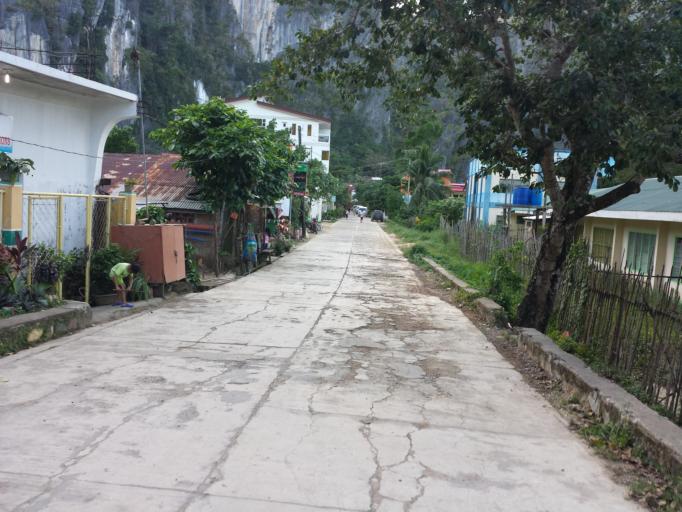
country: PH
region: Mimaropa
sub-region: Province of Palawan
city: El Nido
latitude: 11.1788
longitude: 119.3921
